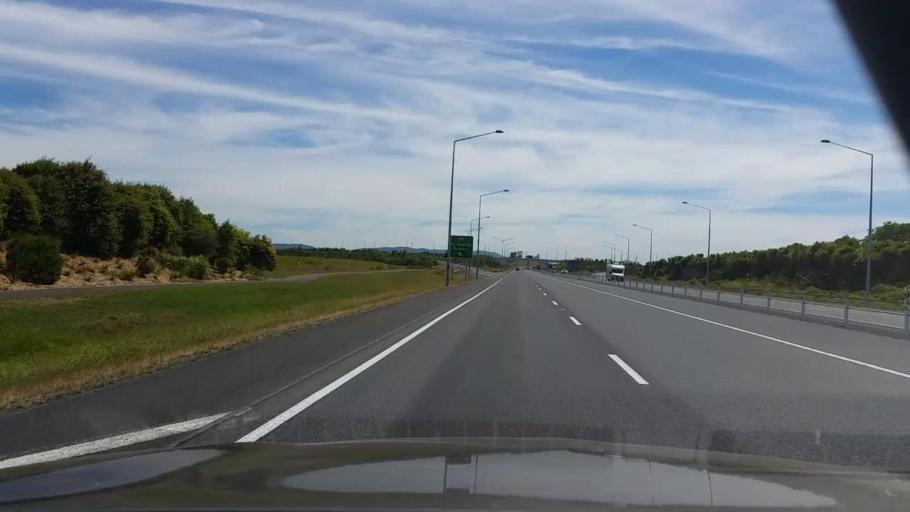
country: NZ
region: Waikato
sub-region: Hamilton City
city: Hamilton
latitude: -37.7379
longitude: 175.2117
